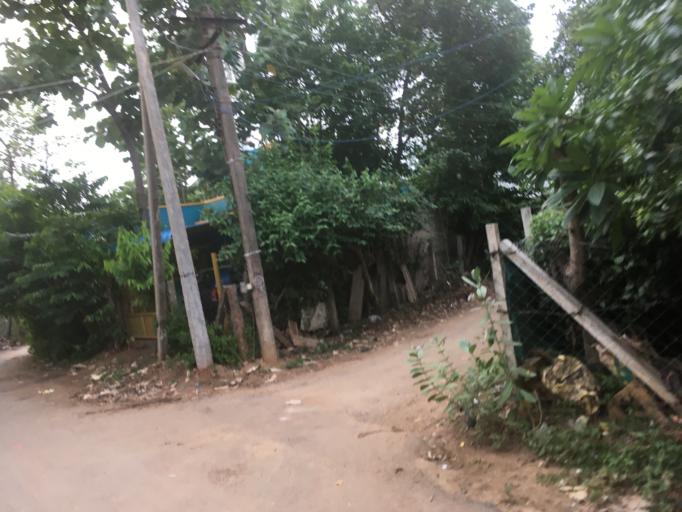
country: IN
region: Tamil Nadu
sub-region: Villupuram
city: Auroville
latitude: 12.0115
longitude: 79.8003
